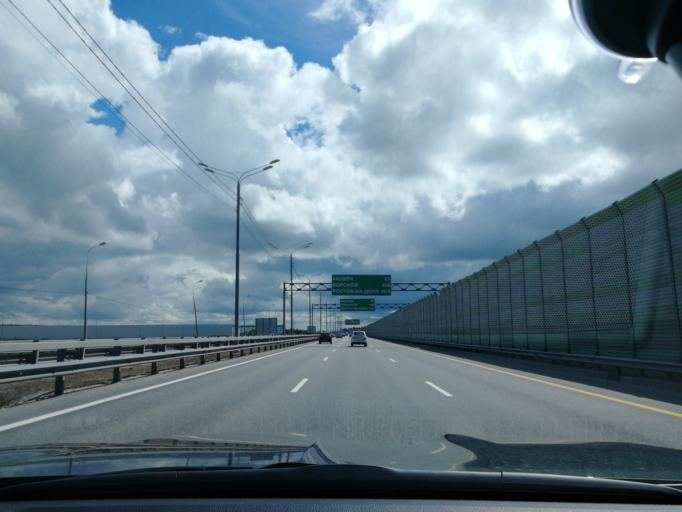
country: RU
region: Moskovskaya
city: Belyye Stolby
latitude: 55.3338
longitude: 37.8093
